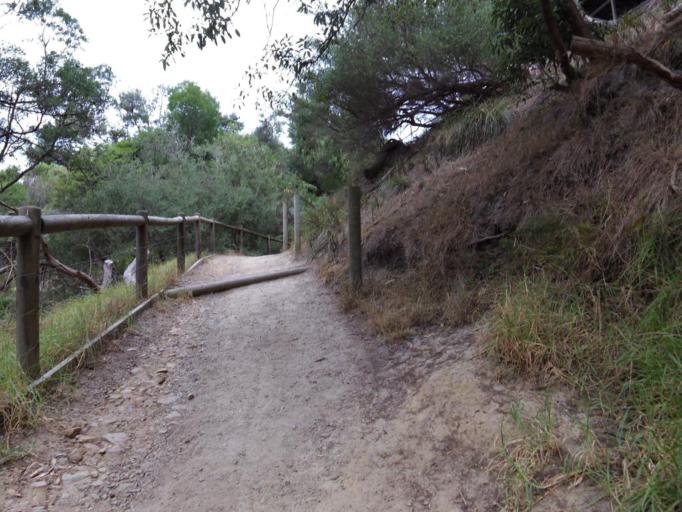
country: AU
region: Victoria
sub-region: Frankston
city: Frankston
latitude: -38.1599
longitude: 145.1105
